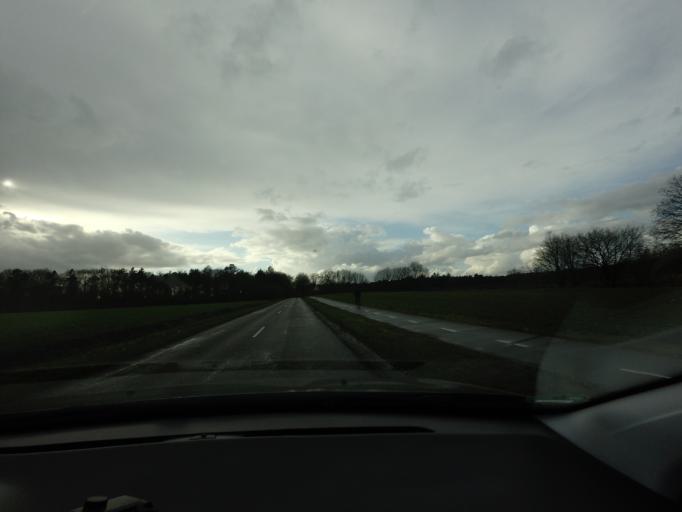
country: NL
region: Drenthe
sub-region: Gemeente Borger-Odoorn
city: Borger
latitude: 52.8425
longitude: 6.6442
